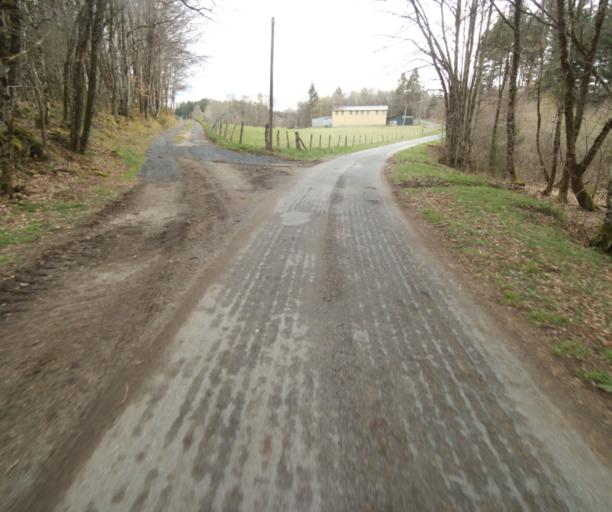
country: FR
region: Limousin
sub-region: Departement de la Correze
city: Correze
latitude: 45.2744
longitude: 1.9510
